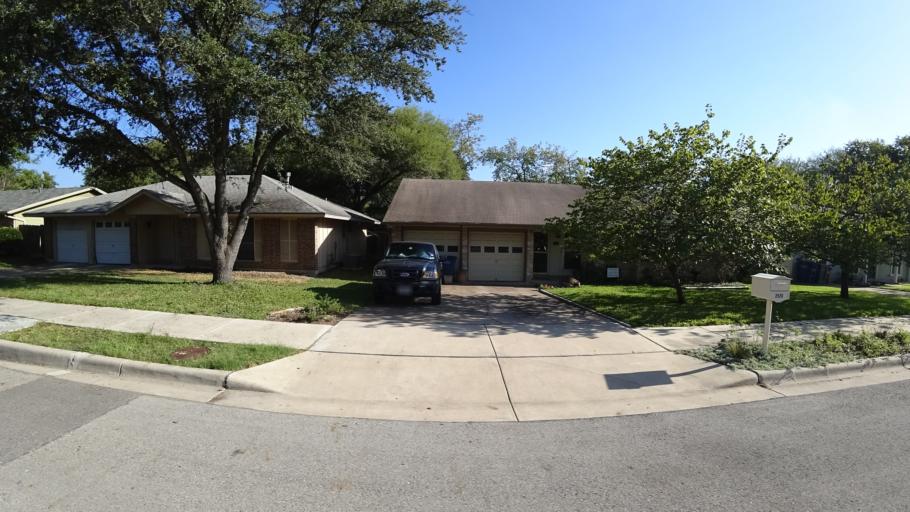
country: US
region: Texas
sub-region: Travis County
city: Rollingwood
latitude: 30.2125
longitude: -97.8107
